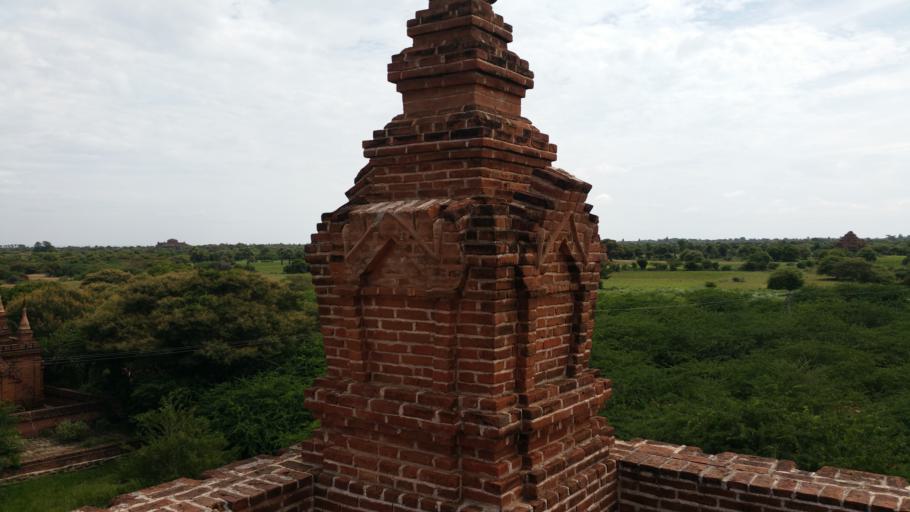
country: MM
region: Magway
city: Chauk
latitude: 21.1459
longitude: 94.8831
